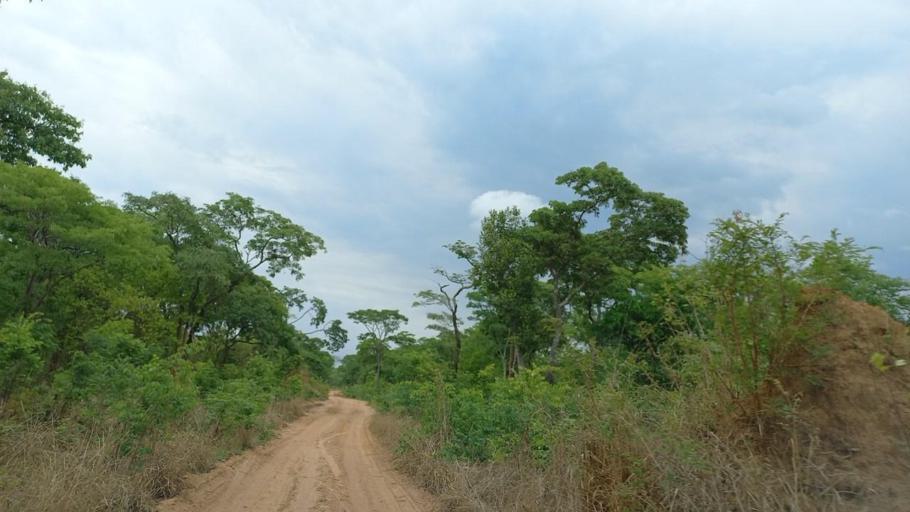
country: ZM
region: North-Western
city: Kalengwa
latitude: -13.5386
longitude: 24.9786
